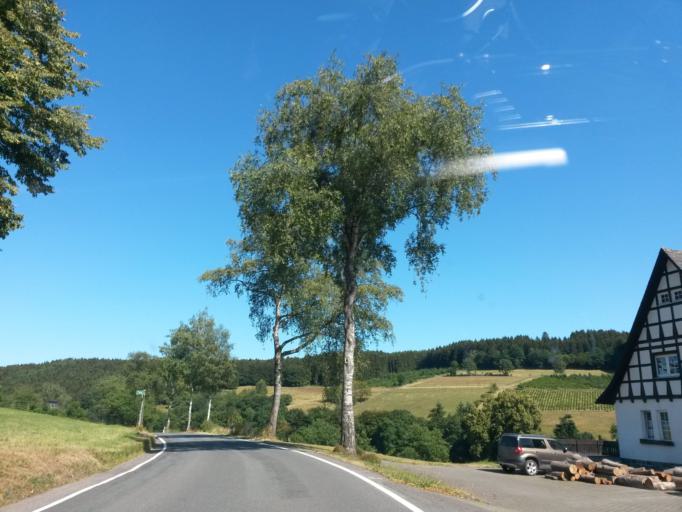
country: DE
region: North Rhine-Westphalia
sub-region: Regierungsbezirk Arnsberg
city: Drolshagen
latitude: 51.0669
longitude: 7.7855
